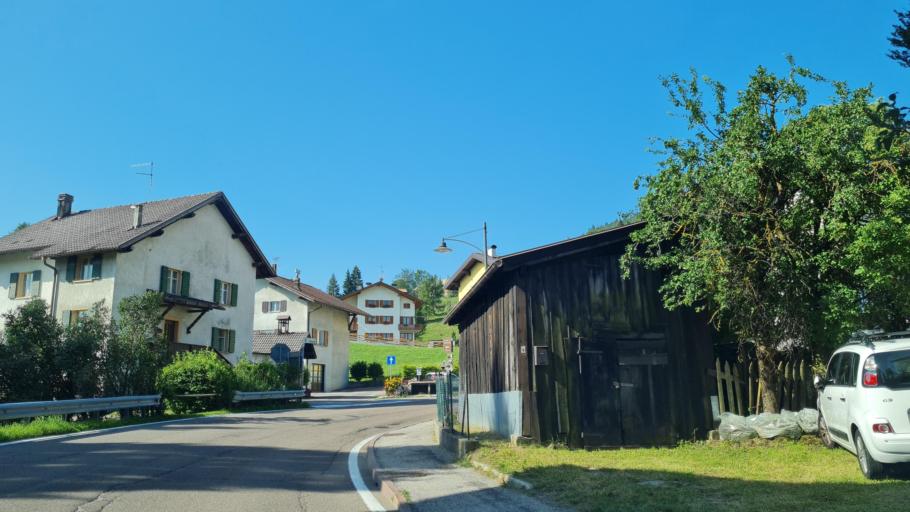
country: IT
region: Trentino-Alto Adige
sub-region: Provincia di Trento
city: Centa San Nicolo
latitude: 45.9334
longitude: 11.2261
